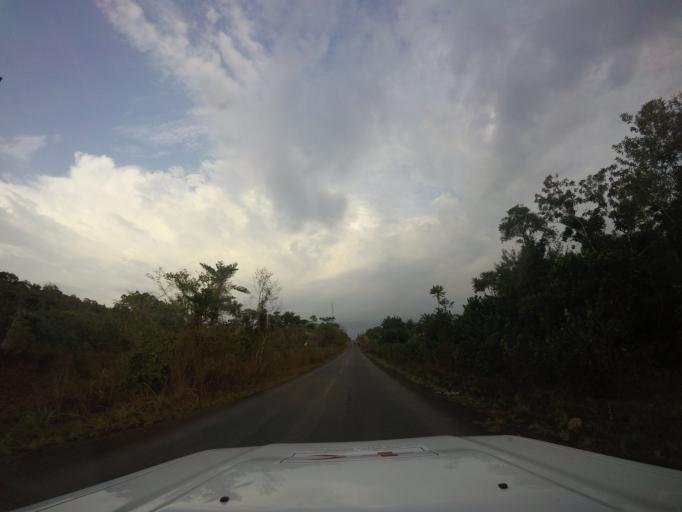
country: LR
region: Bomi
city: Tubmanburg
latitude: 6.6933
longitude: -10.8948
